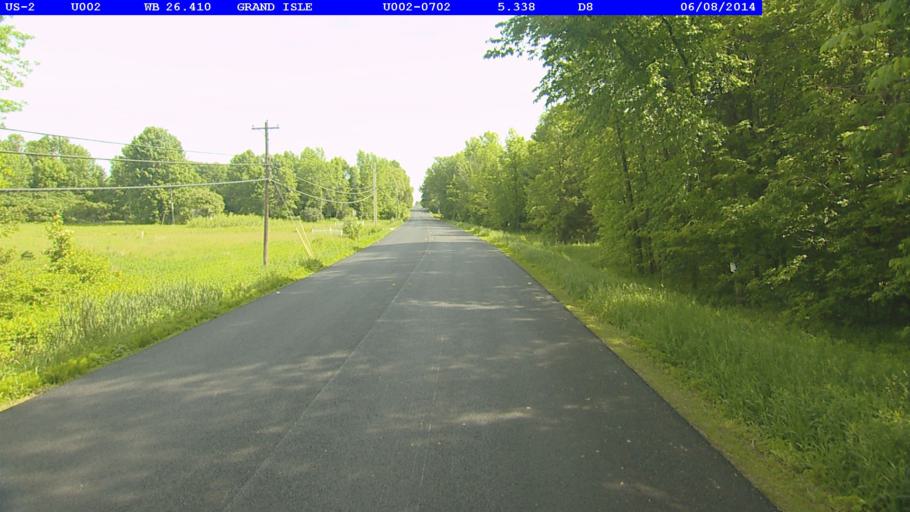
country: US
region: New York
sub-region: Clinton County
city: Cumberland Head
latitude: 44.6923
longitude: -73.3075
